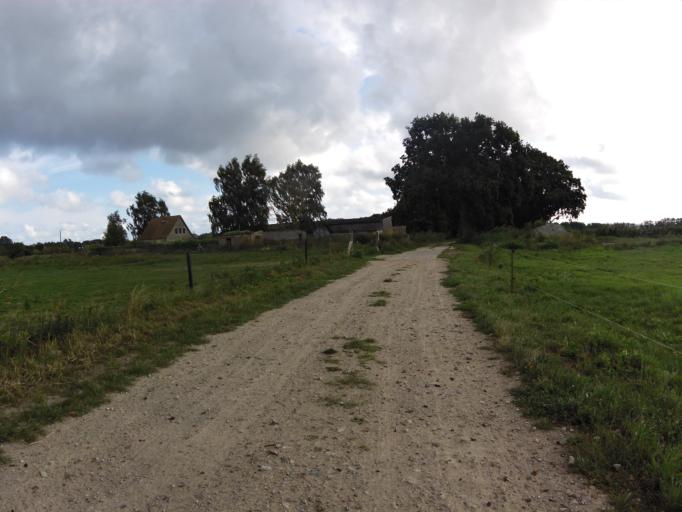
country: DE
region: Mecklenburg-Vorpommern
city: Loddin
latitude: 53.9813
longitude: 14.0646
